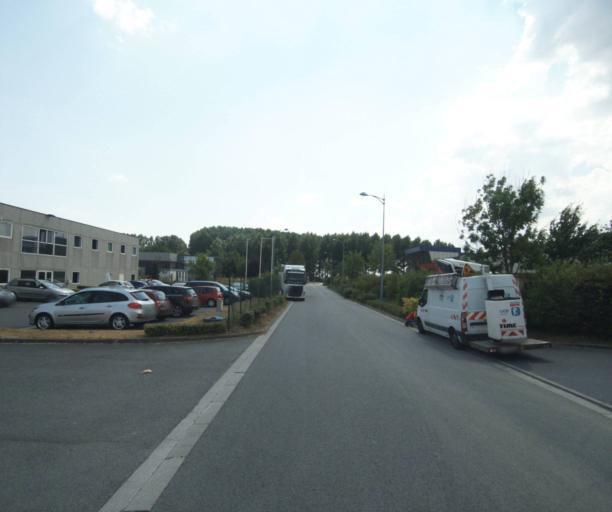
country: FR
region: Nord-Pas-de-Calais
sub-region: Departement du Nord
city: Comines
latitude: 50.7524
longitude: 2.9947
